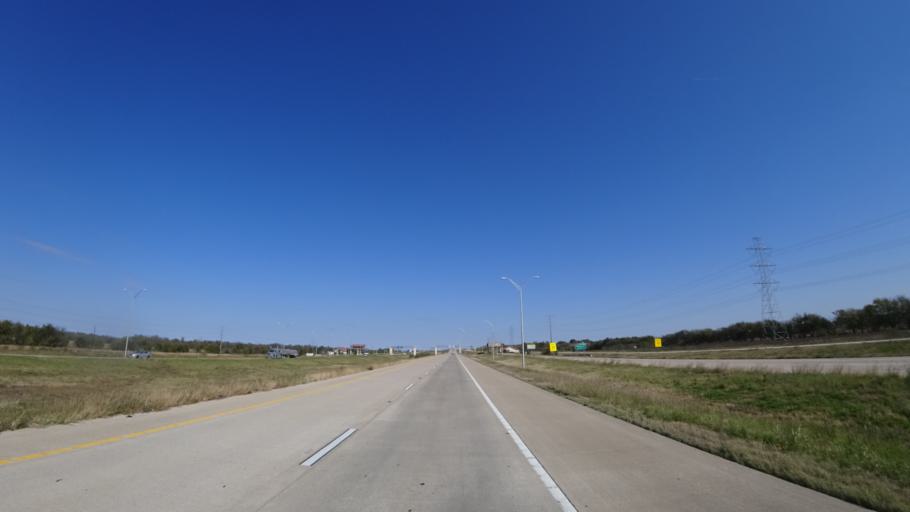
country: US
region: Texas
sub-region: Travis County
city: Garfield
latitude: 30.1675
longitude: -97.6472
